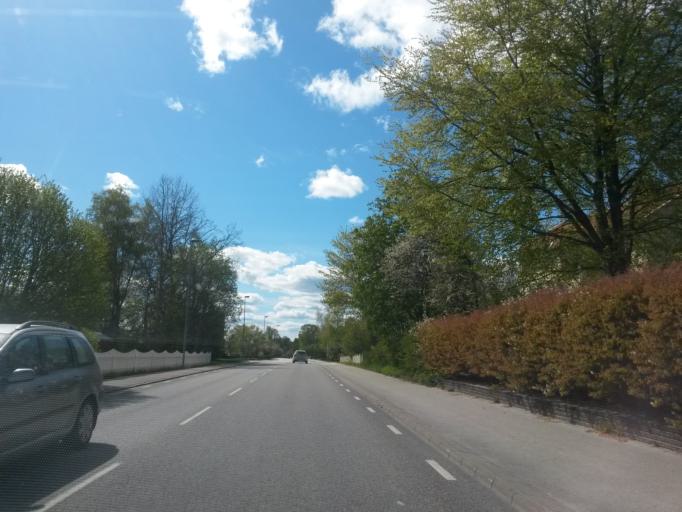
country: SE
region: Vaestra Goetaland
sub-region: Herrljunga Kommun
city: Herrljunga
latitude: 58.0779
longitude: 13.0105
